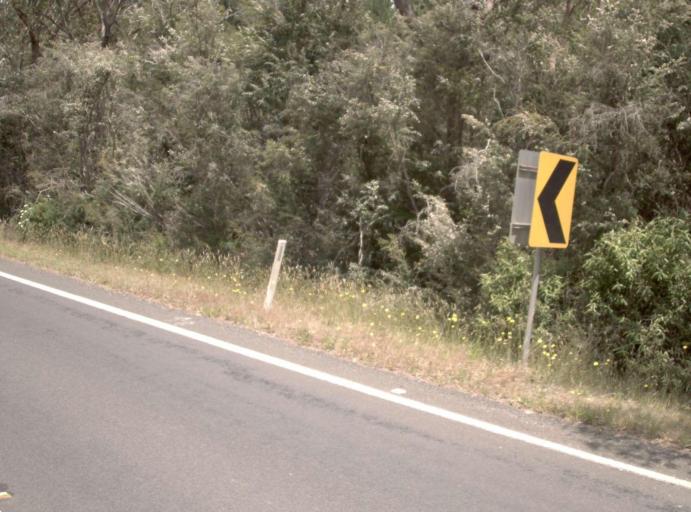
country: AU
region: Victoria
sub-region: Latrobe
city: Traralgon
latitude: -38.2789
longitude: 146.6936
